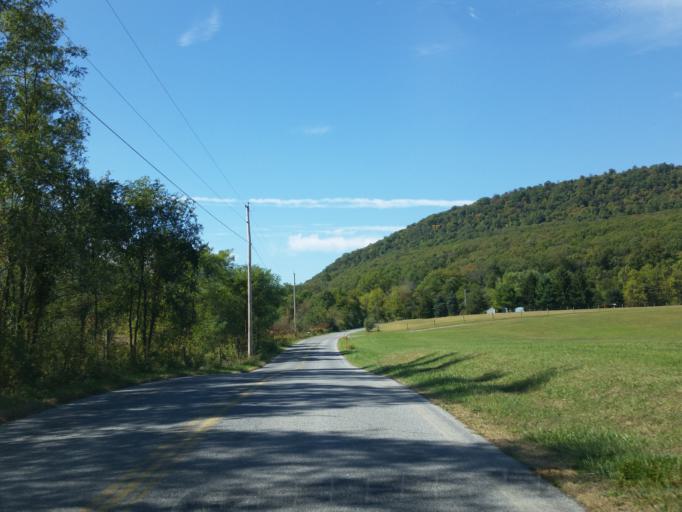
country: US
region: Pennsylvania
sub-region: Lebanon County
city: Jonestown
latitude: 40.4732
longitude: -76.5094
